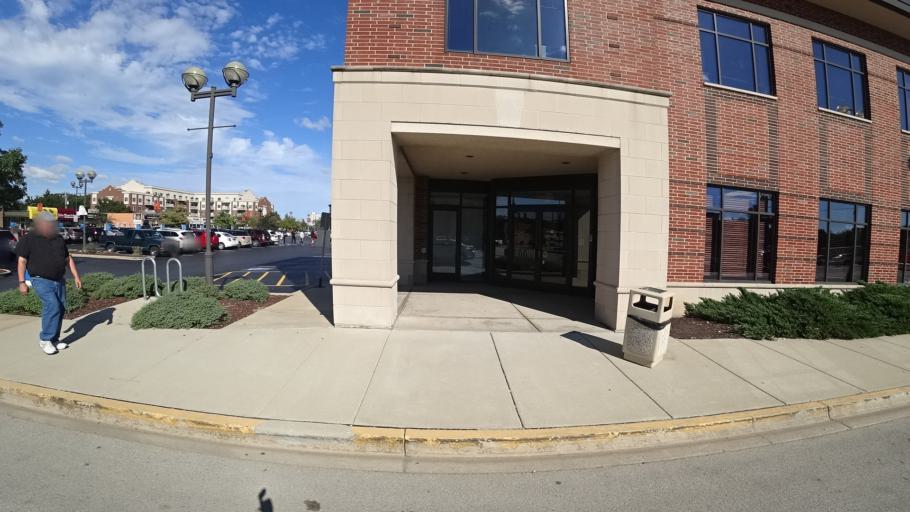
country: US
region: Illinois
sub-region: Cook County
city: Oak Lawn
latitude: 41.7194
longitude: -87.7505
